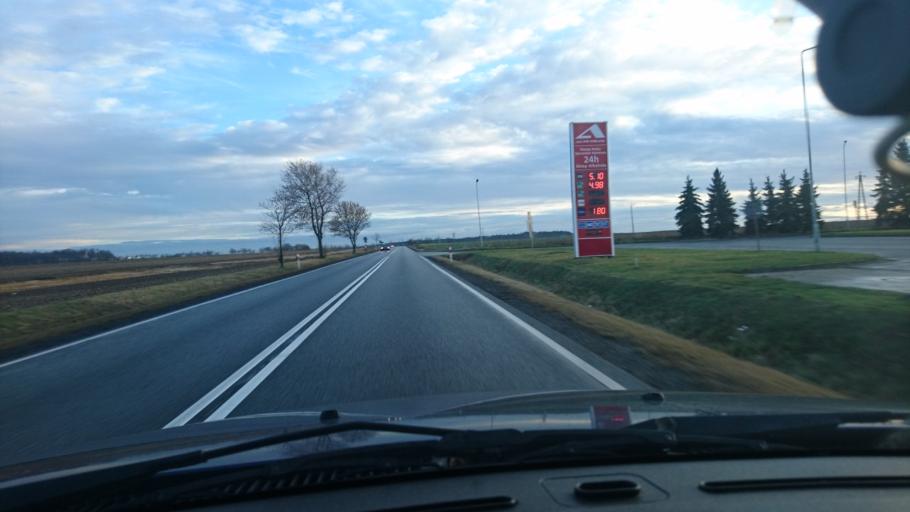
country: PL
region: Greater Poland Voivodeship
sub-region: Powiat kepinski
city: Baranow
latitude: 51.2496
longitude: 18.0158
